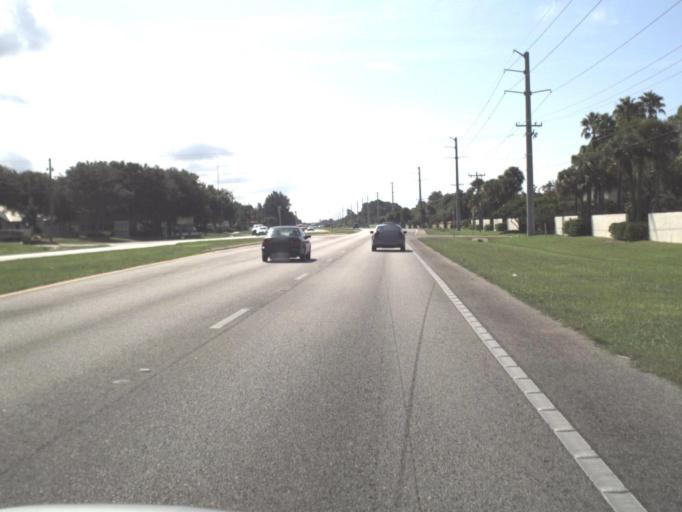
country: US
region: Florida
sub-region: Sarasota County
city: Laurel
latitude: 27.1671
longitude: -82.4768
